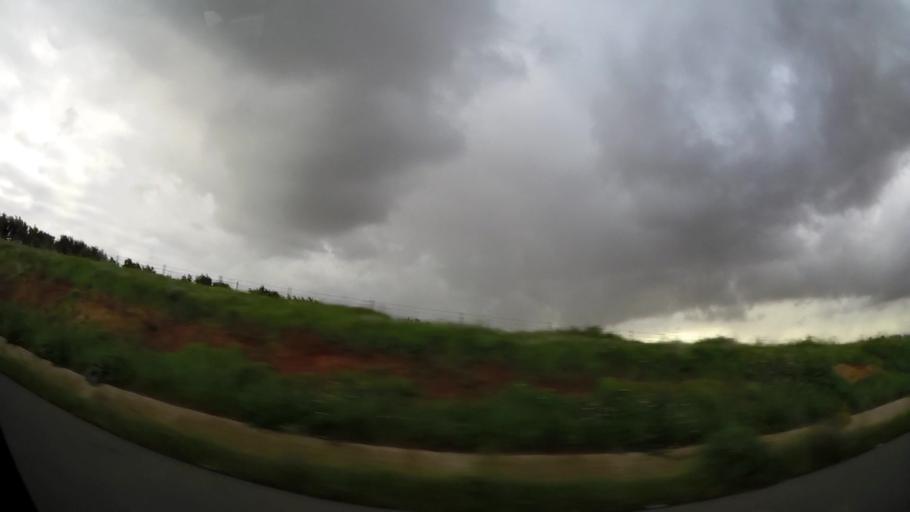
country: MA
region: Grand Casablanca
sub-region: Mediouna
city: Tit Mellil
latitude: 33.5789
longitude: -7.4532
